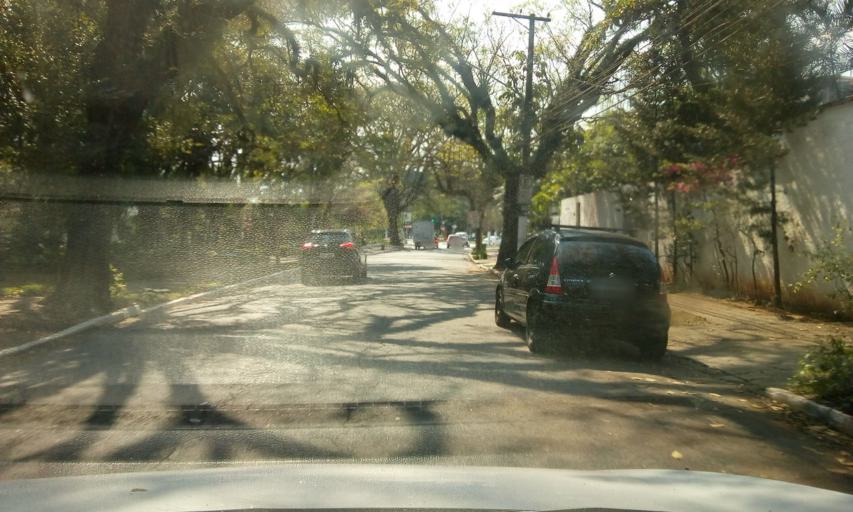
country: BR
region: Sao Paulo
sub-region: Osasco
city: Osasco
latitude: -23.5253
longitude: -46.7186
